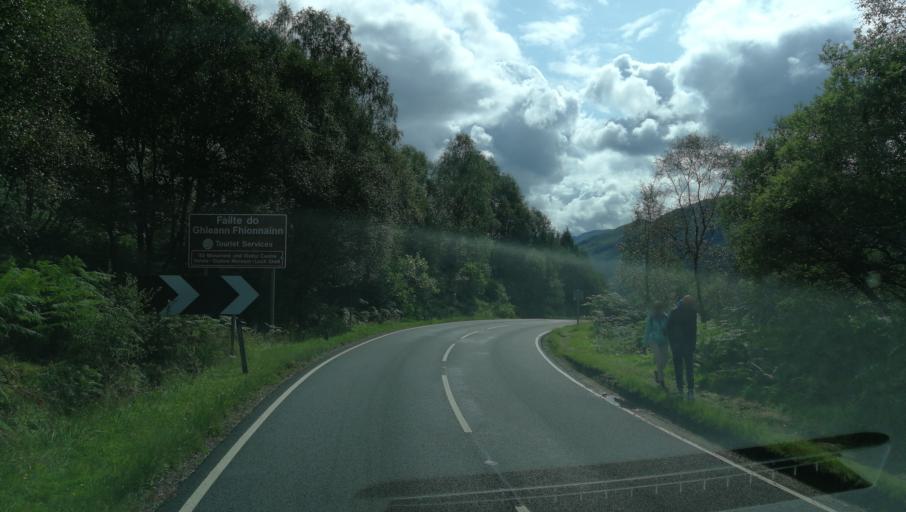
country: GB
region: Scotland
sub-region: Highland
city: Fort William
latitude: 56.8764
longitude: -5.4612
